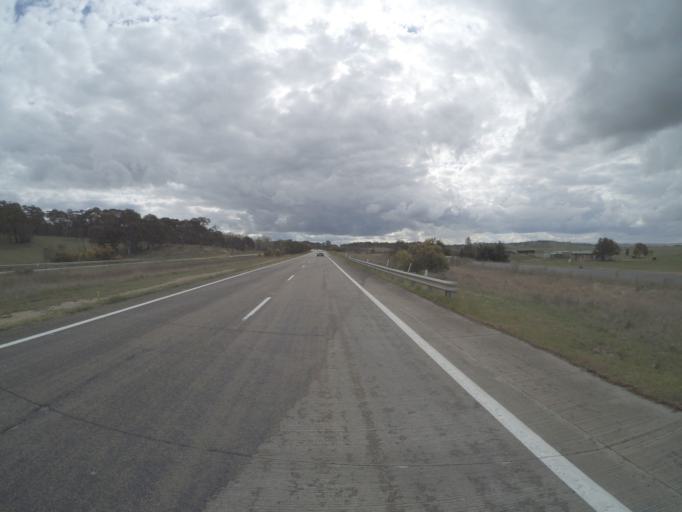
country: AU
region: New South Wales
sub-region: Goulburn Mulwaree
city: Goulburn
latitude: -34.8054
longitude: 149.5147
